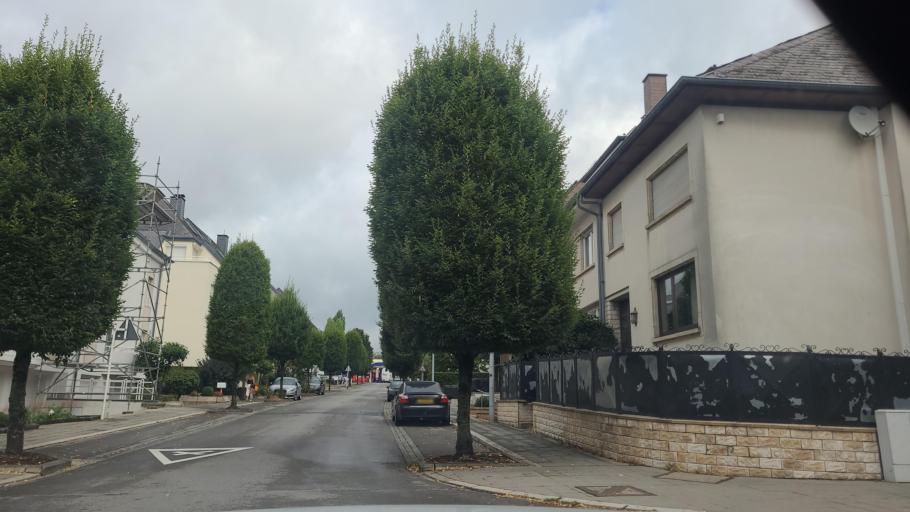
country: LU
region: Luxembourg
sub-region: Canton de Luxembourg
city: Luxembourg
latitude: 49.6040
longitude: 6.1008
